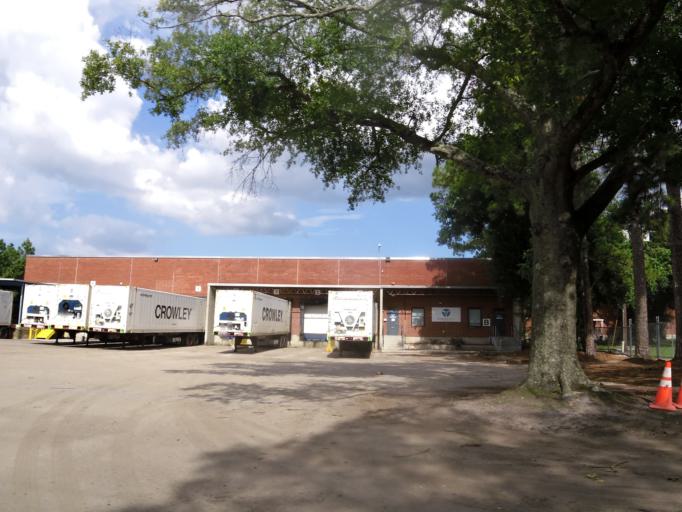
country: US
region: Florida
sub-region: Duval County
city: Jacksonville
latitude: 30.3632
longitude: -81.6954
